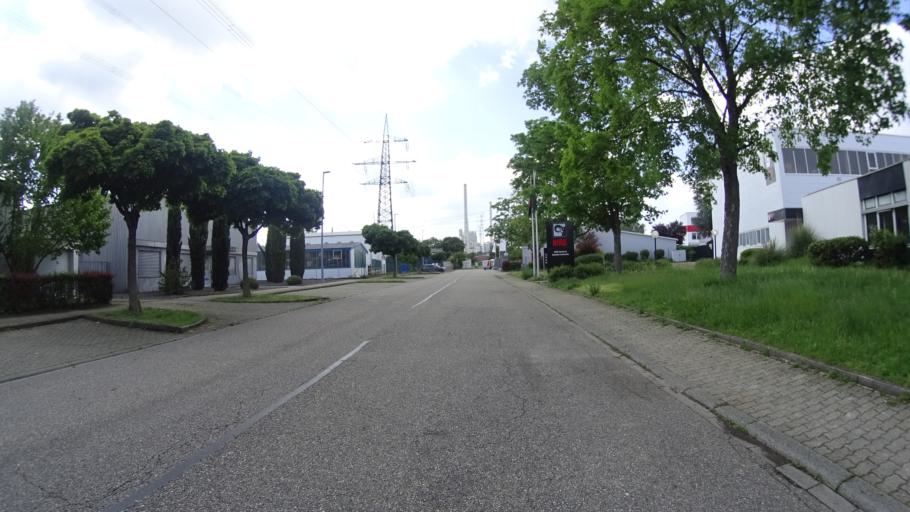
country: DE
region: Baden-Wuerttemberg
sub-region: Karlsruhe Region
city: Rheinstetten
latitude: 49.0088
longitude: 8.3192
